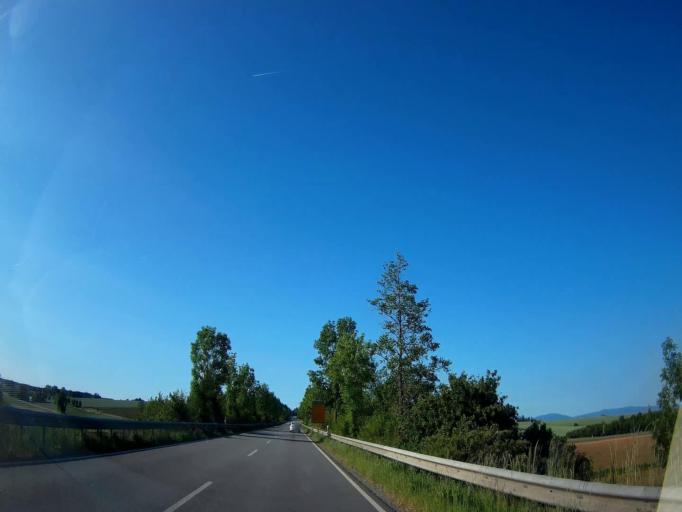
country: DE
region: Bavaria
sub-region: Lower Bavaria
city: Pilsting
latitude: 48.7457
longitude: 12.6599
